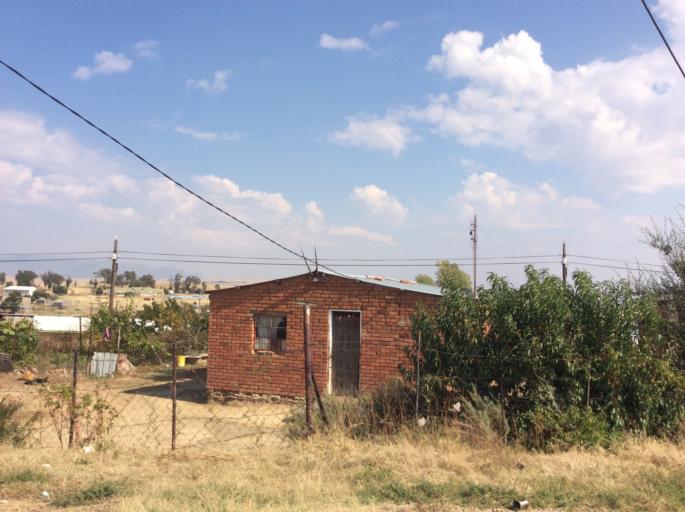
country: LS
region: Mafeteng
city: Mafeteng
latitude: -29.9822
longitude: 27.0087
